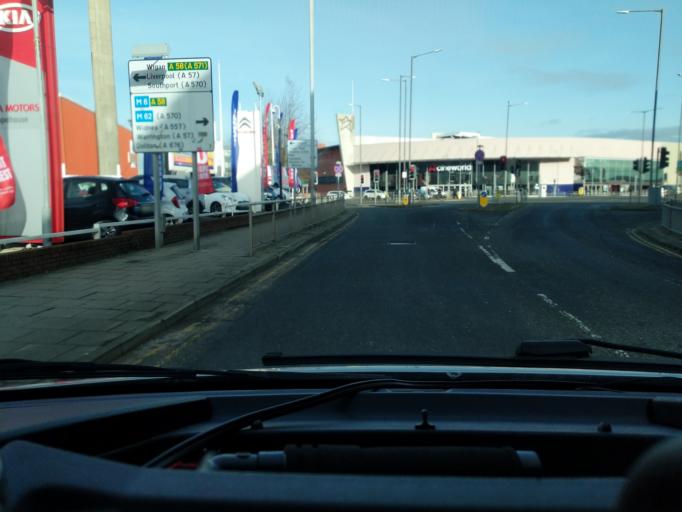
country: GB
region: England
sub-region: St. Helens
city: St Helens
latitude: 53.4504
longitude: -2.7410
